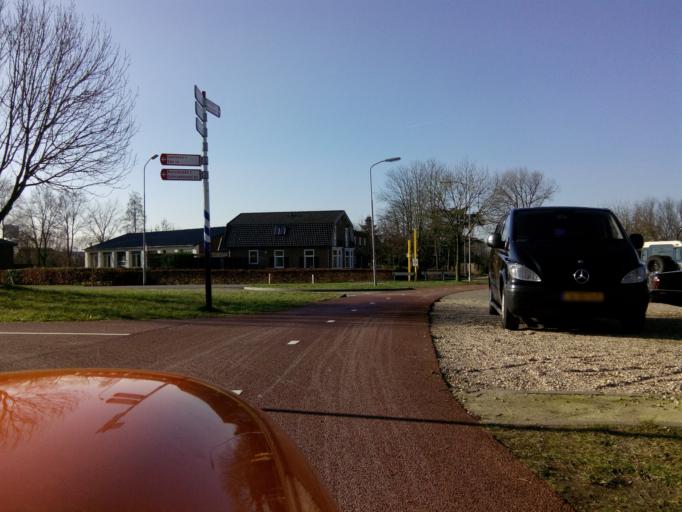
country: NL
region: Gelderland
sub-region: Gemeente Barneveld
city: Barneveld
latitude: 52.1325
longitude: 5.5687
